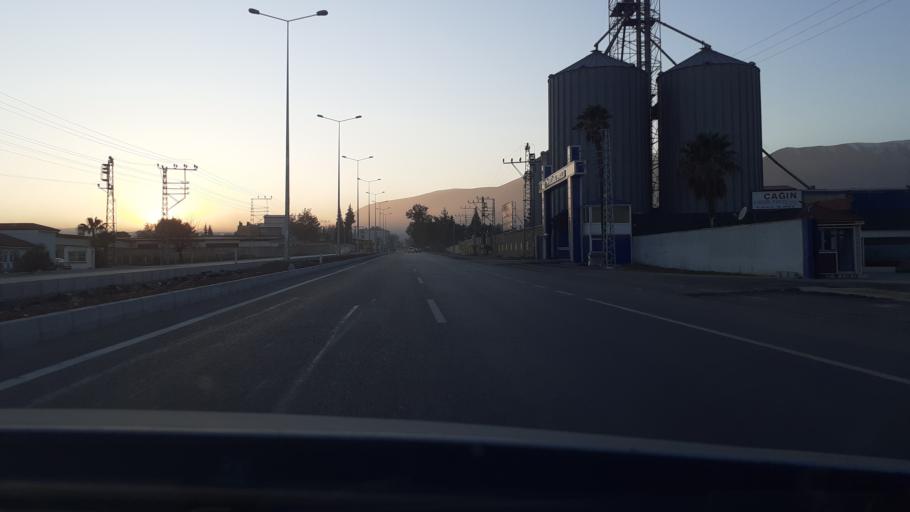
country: TR
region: Hatay
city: Kirikhan
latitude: 36.5009
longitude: 36.3804
